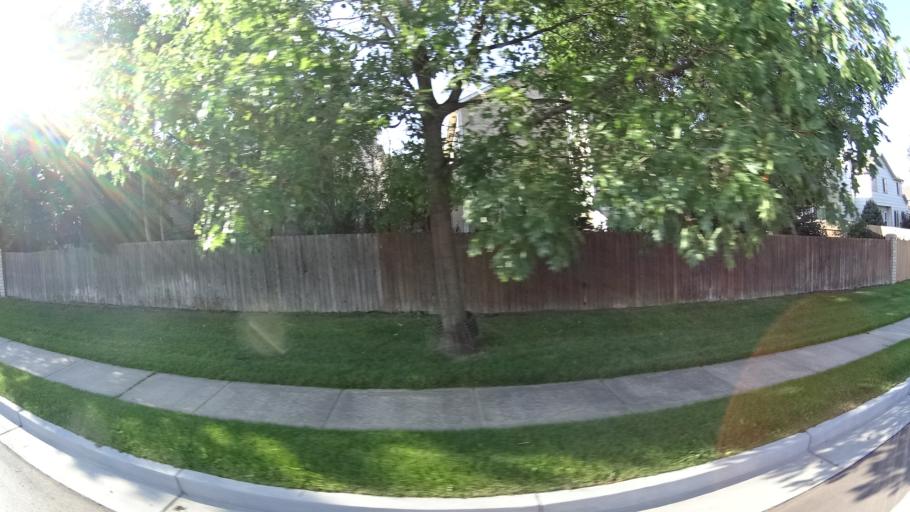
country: US
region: Colorado
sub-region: El Paso County
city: Air Force Academy
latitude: 38.9493
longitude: -104.7875
